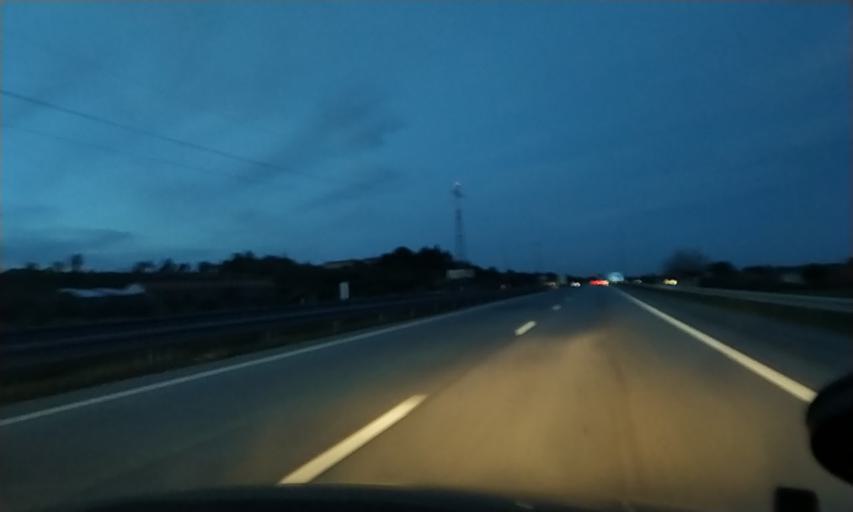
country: PT
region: Castelo Branco
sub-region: Castelo Branco
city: Castelo Branco
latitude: 39.8575
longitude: -7.5000
